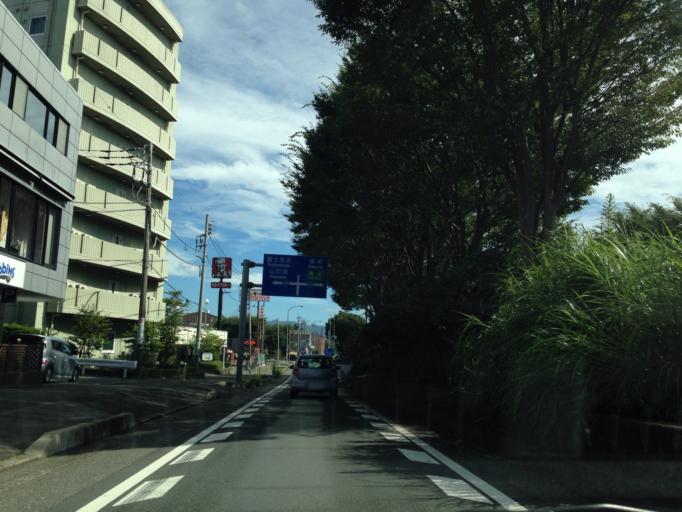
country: JP
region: Shizuoka
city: Gotemba
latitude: 35.3114
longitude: 138.9268
